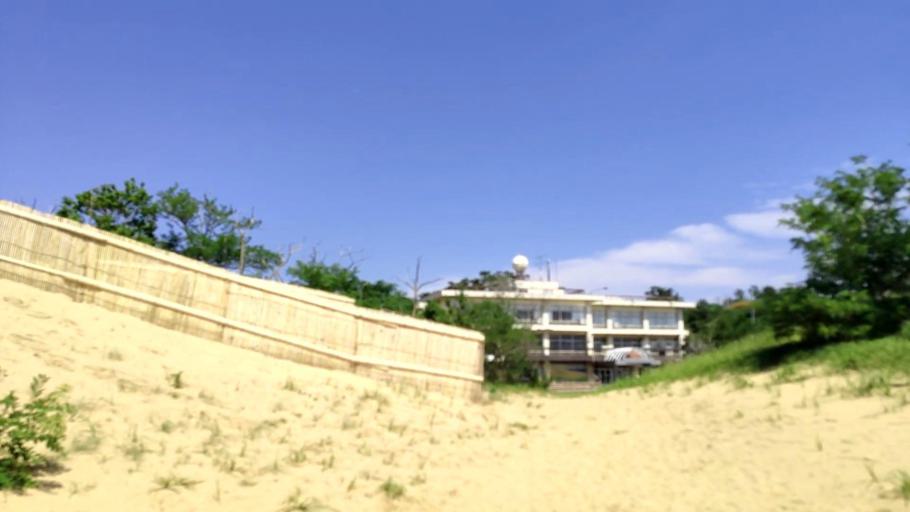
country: JP
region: Tottori
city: Tottori
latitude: 35.5417
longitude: 134.2358
